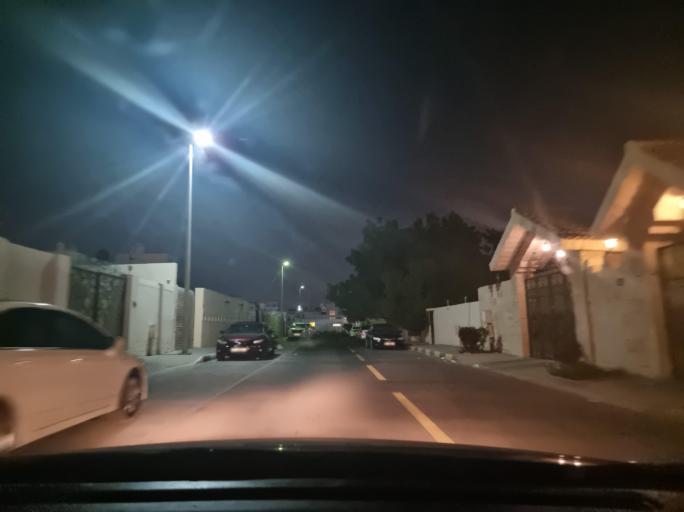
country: AE
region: Ash Shariqah
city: Sharjah
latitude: 25.3691
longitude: 55.4239
